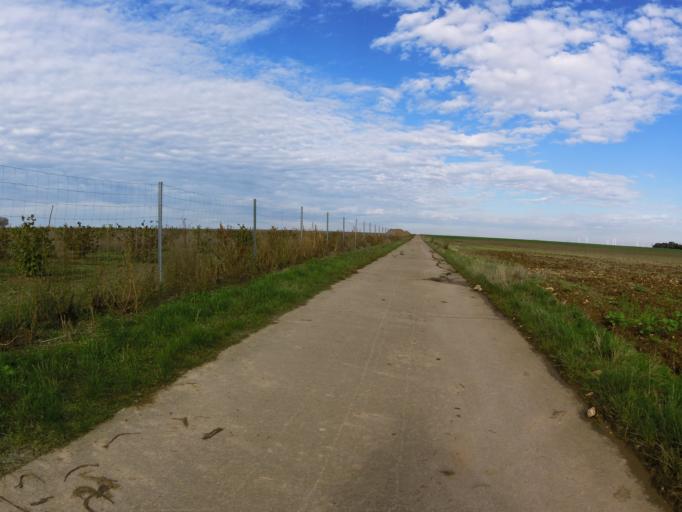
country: DE
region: Bavaria
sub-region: Regierungsbezirk Unterfranken
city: Sommerhausen
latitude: 49.7136
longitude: 10.0688
